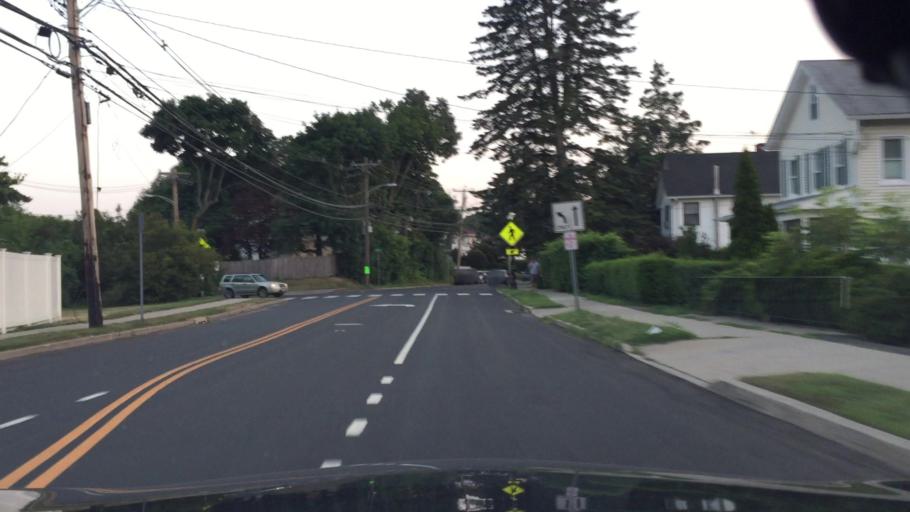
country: US
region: Connecticut
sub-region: Fairfield County
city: Norwalk
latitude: 41.0966
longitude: -73.4258
